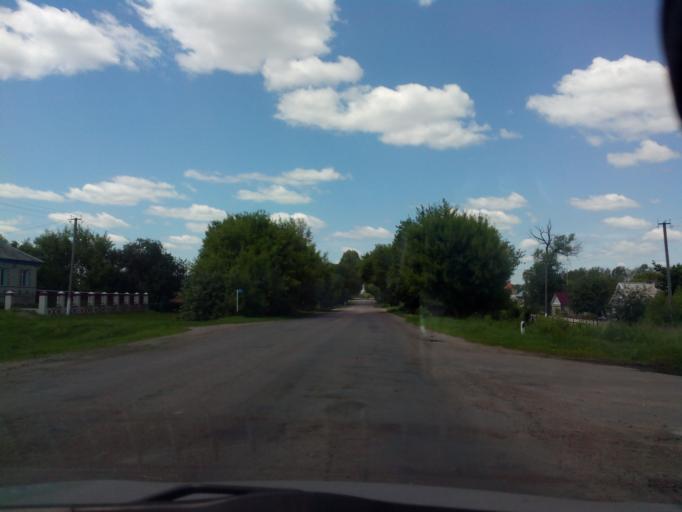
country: RU
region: Voronezj
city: Ternovka
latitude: 51.6749
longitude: 41.6155
